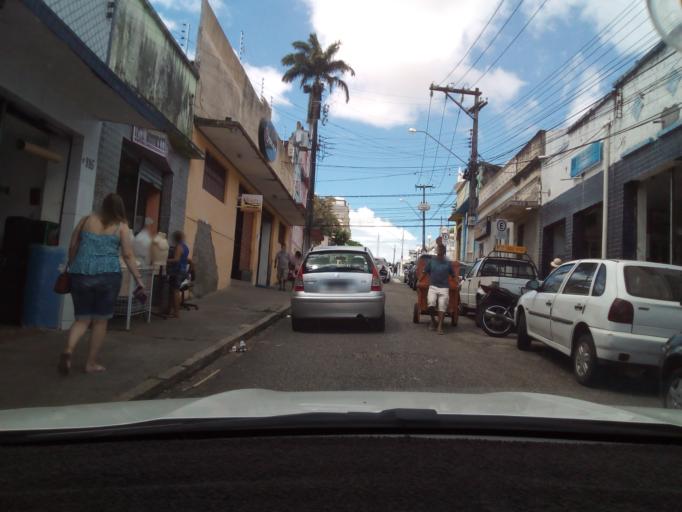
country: BR
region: Paraiba
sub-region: Joao Pessoa
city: Joao Pessoa
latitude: -7.1217
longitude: -34.8855
